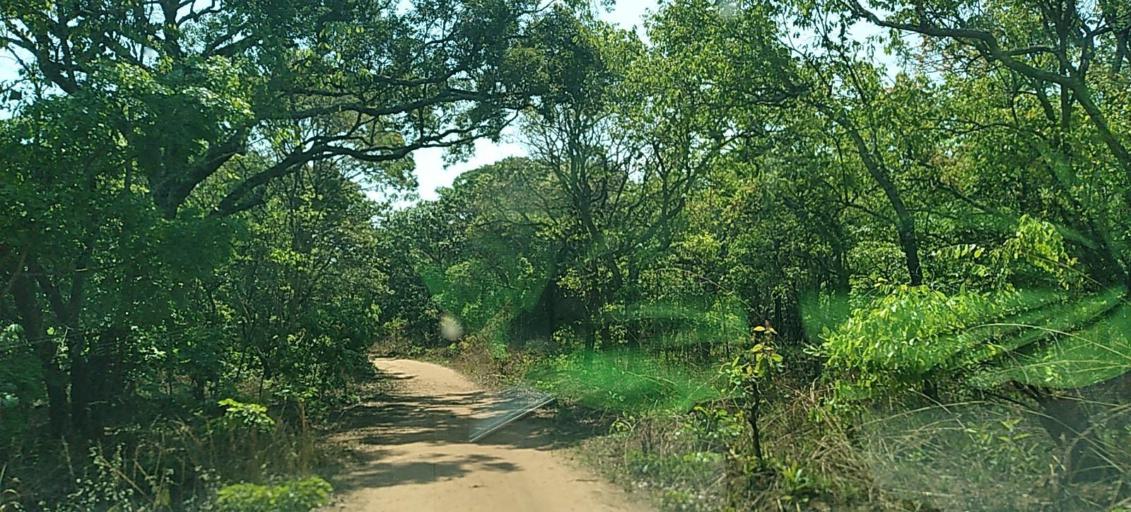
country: CD
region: Katanga
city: Kolwezi
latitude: -11.2759
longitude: 25.1154
